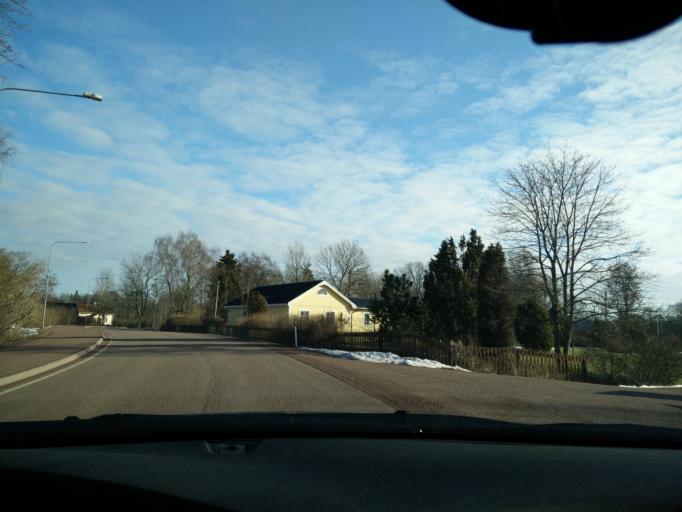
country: AX
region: Alands landsbygd
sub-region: Eckeroe
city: Eckeroe
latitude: 60.2263
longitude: 19.5530
